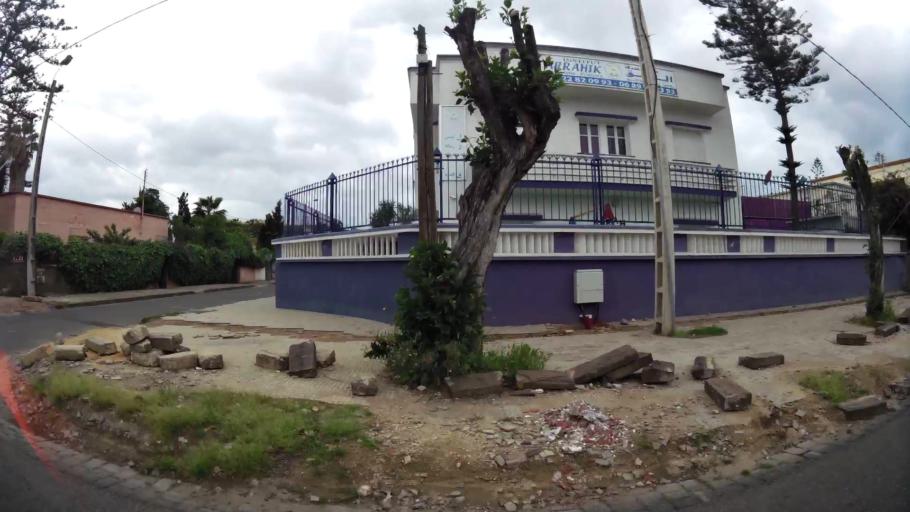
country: MA
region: Grand Casablanca
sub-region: Casablanca
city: Casablanca
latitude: 33.5591
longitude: -7.6119
